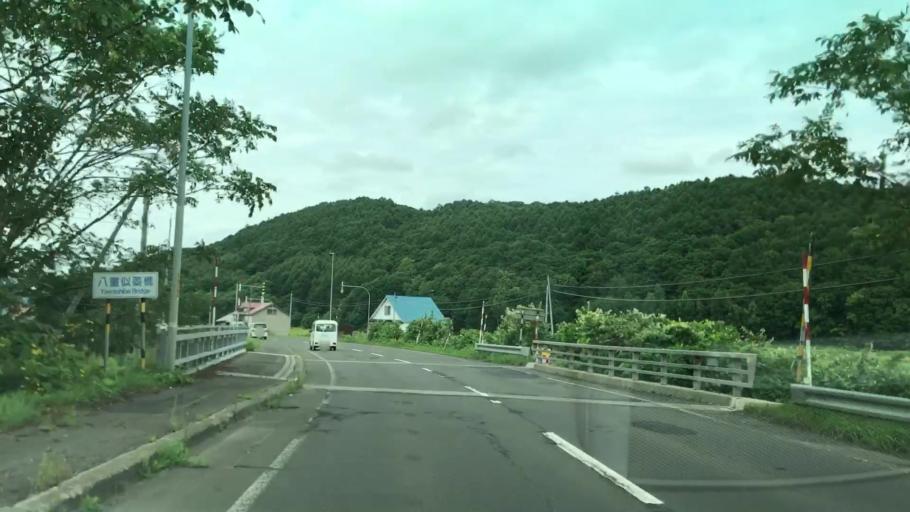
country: JP
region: Hokkaido
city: Iwanai
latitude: 42.9645
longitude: 140.6919
